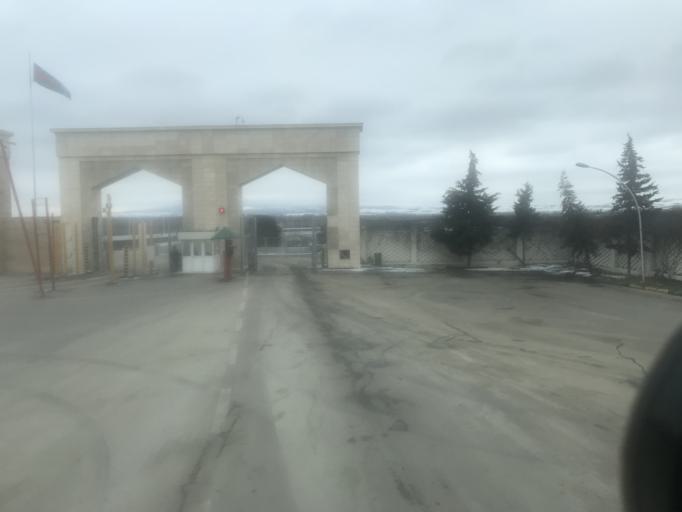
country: AZ
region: Qusar
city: Samur
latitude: 41.6376
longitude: 48.4195
